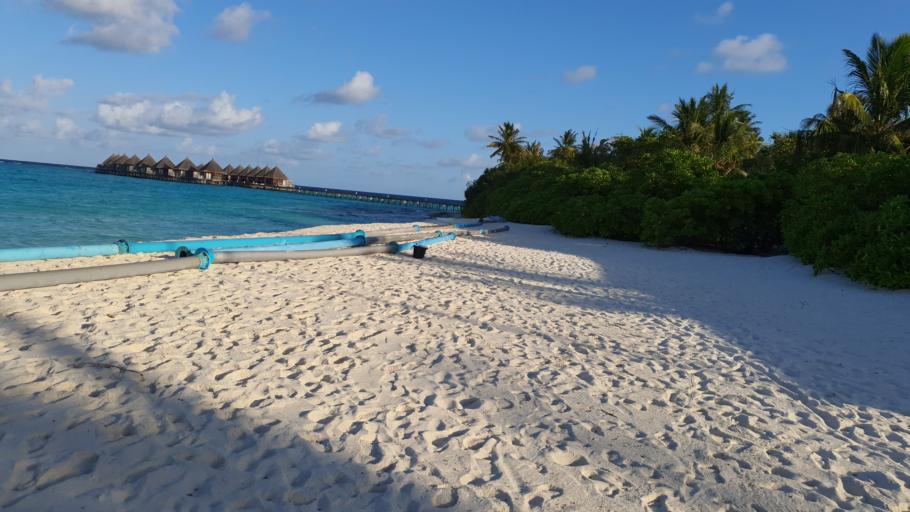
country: MV
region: North Central
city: Mahibadhoo
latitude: 3.6516
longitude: 72.8219
